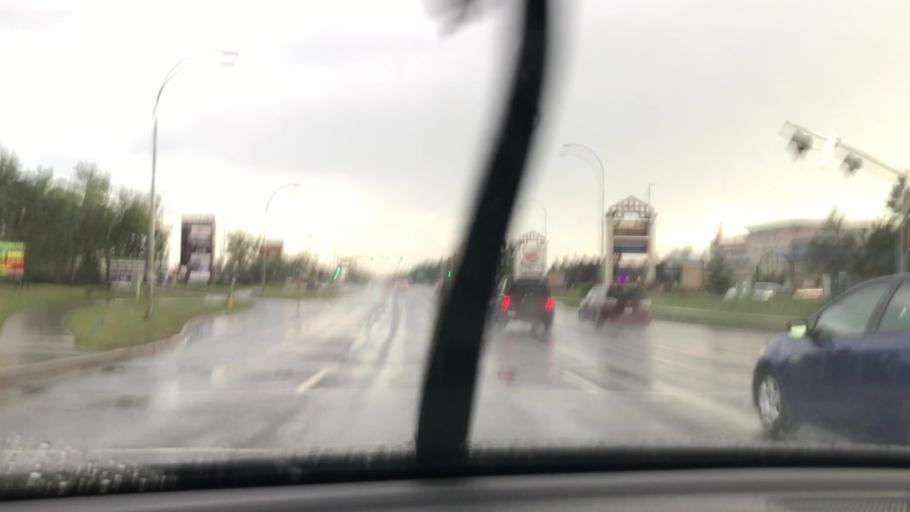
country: CA
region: Alberta
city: Edmonton
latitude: 53.4797
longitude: -113.4956
